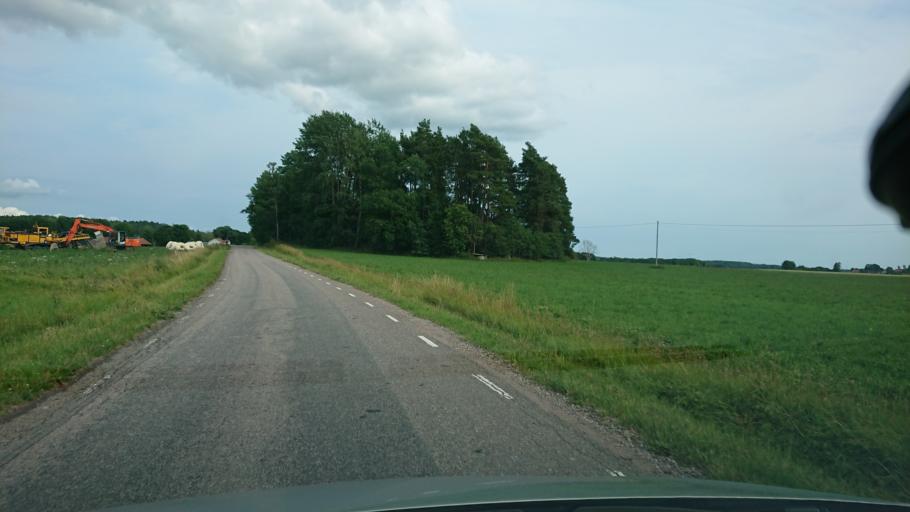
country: SE
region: Uppsala
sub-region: Osthammars Kommun
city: Bjorklinge
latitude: 59.9864
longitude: 17.5508
